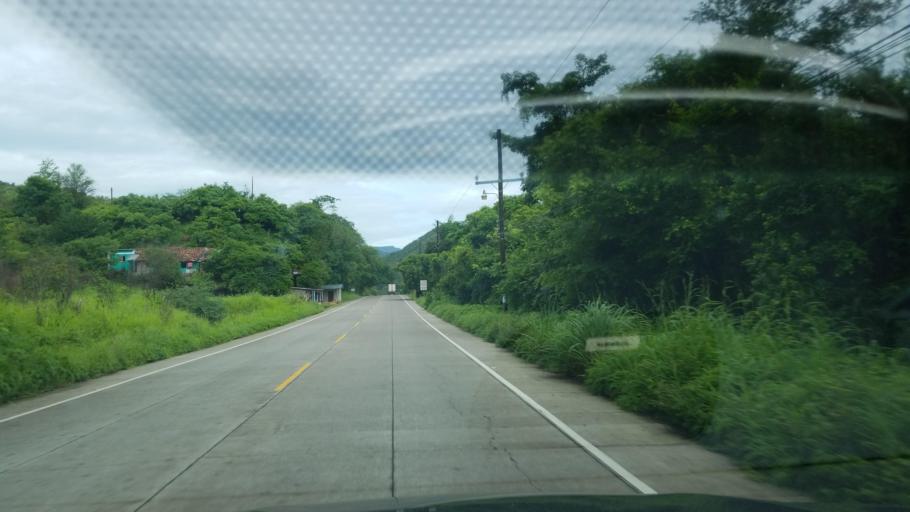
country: HN
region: Francisco Morazan
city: El Porvenir
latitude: 13.6860
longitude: -87.3395
